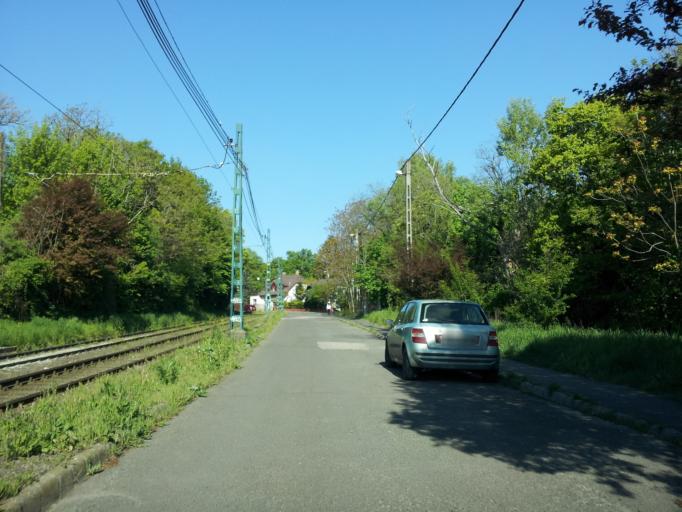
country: HU
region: Pest
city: Budakeszi
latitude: 47.5395
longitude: 18.9708
